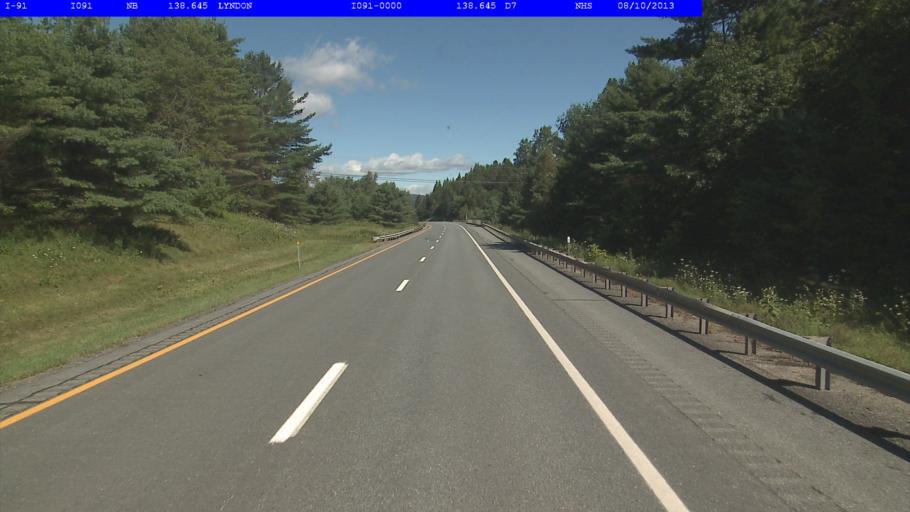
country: US
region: Vermont
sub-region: Caledonia County
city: Lyndonville
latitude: 44.5370
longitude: -72.0184
